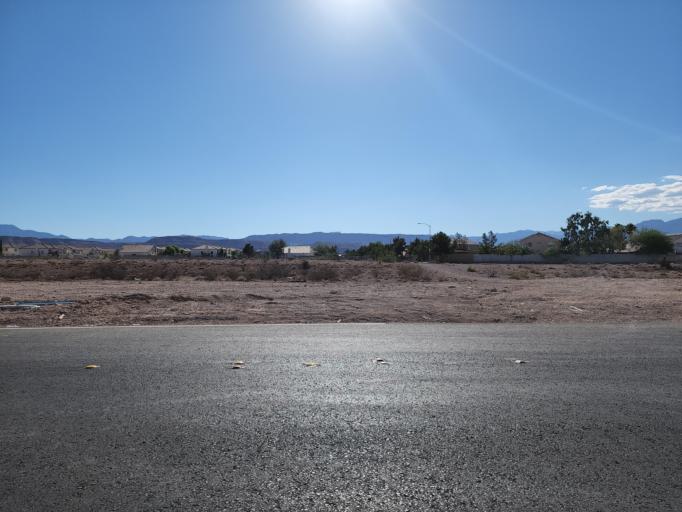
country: US
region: Nevada
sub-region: Clark County
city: Spring Valley
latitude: 36.0813
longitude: -115.2702
